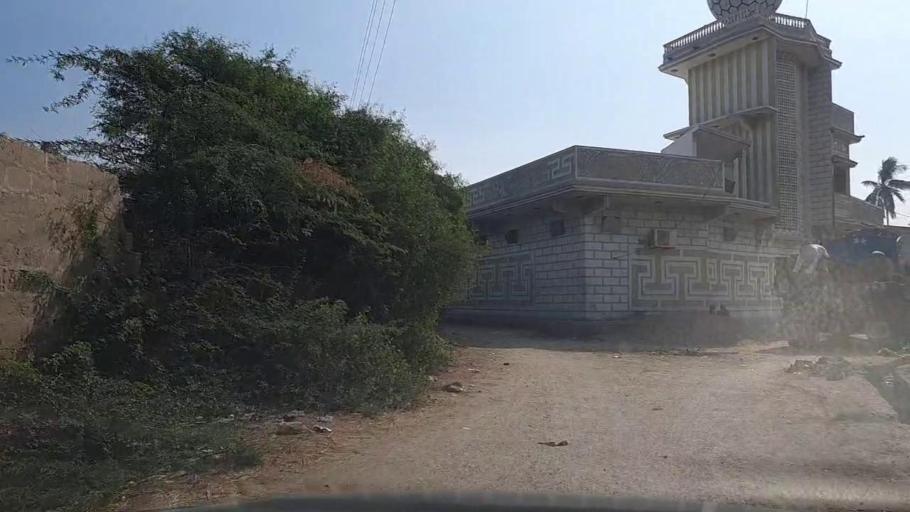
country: PK
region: Sindh
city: Thatta
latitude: 24.5664
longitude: 67.8906
